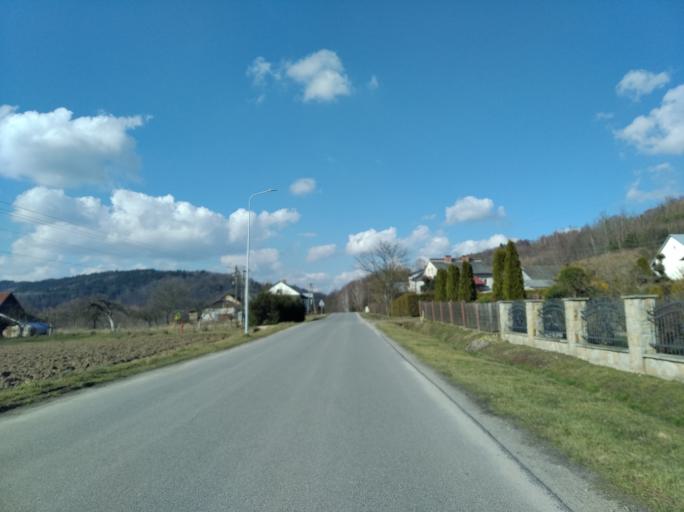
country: PL
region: Subcarpathian Voivodeship
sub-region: Powiat strzyzowski
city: Frysztak
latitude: 49.8456
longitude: 21.6274
